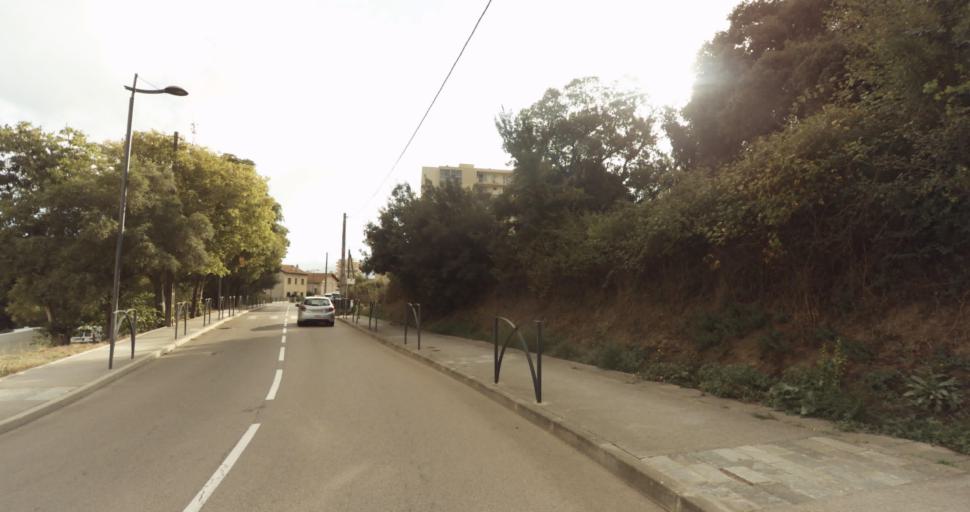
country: FR
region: Corsica
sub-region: Departement de la Corse-du-Sud
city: Ajaccio
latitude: 41.9289
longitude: 8.7285
